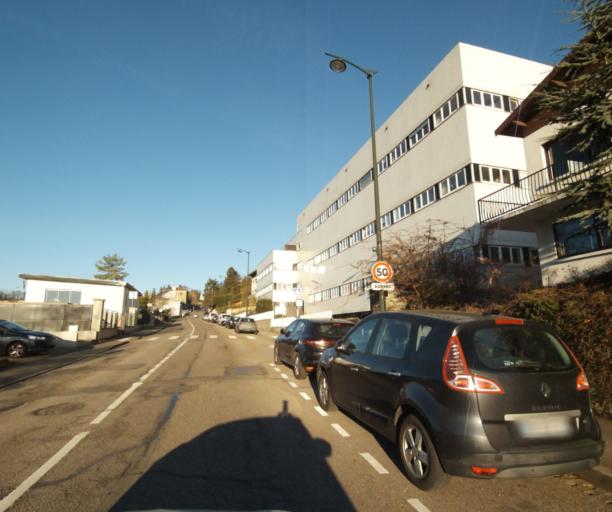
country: FR
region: Lorraine
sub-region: Departement de Meurthe-et-Moselle
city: Laxou
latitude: 48.6881
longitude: 6.1411
